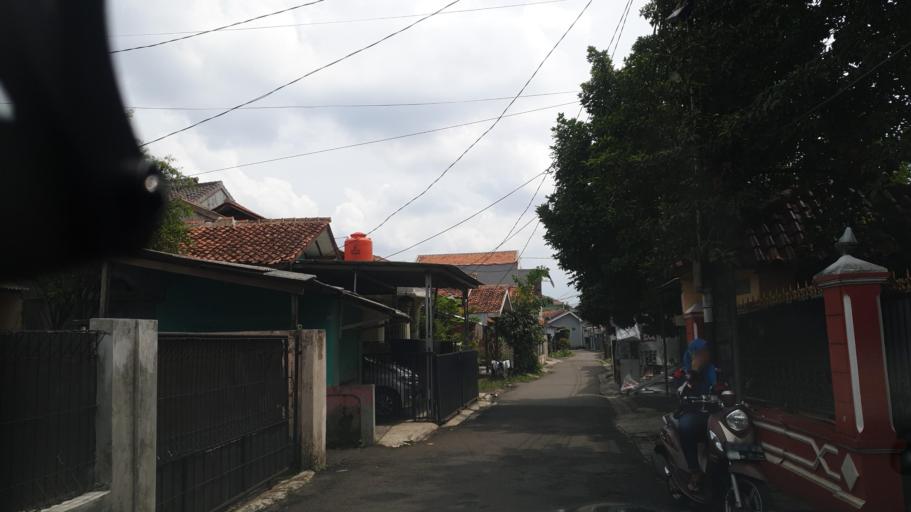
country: ID
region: West Java
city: Pamulang
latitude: -6.3394
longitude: 106.7688
